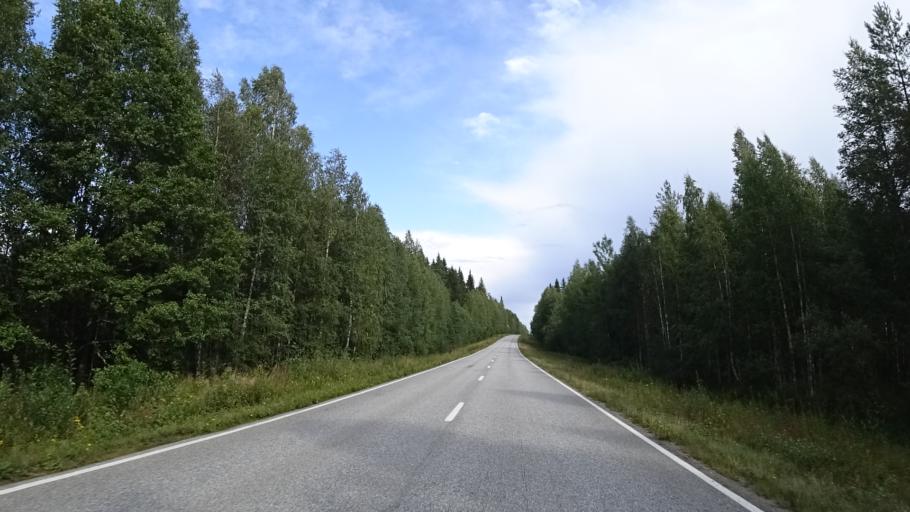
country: FI
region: North Karelia
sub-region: Joensuu
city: Ilomantsi
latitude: 62.6230
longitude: 31.1327
